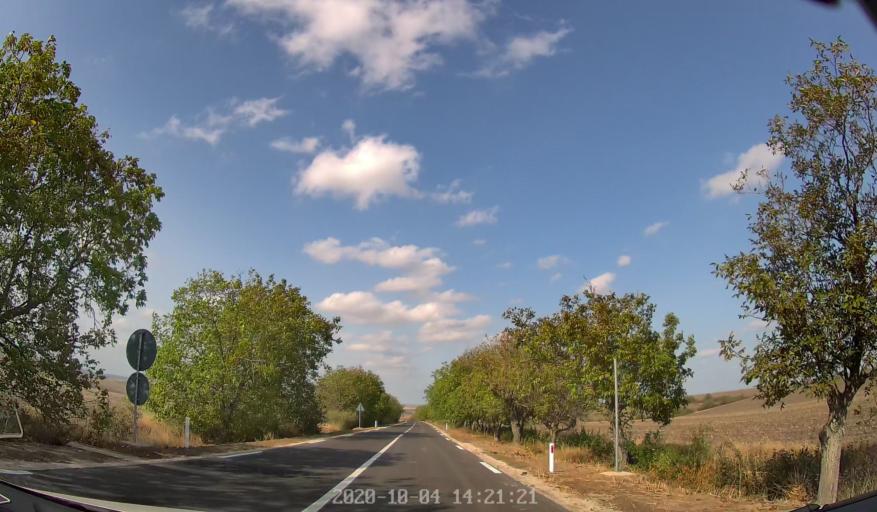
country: MD
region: Rezina
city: Saharna
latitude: 47.5840
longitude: 28.9559
